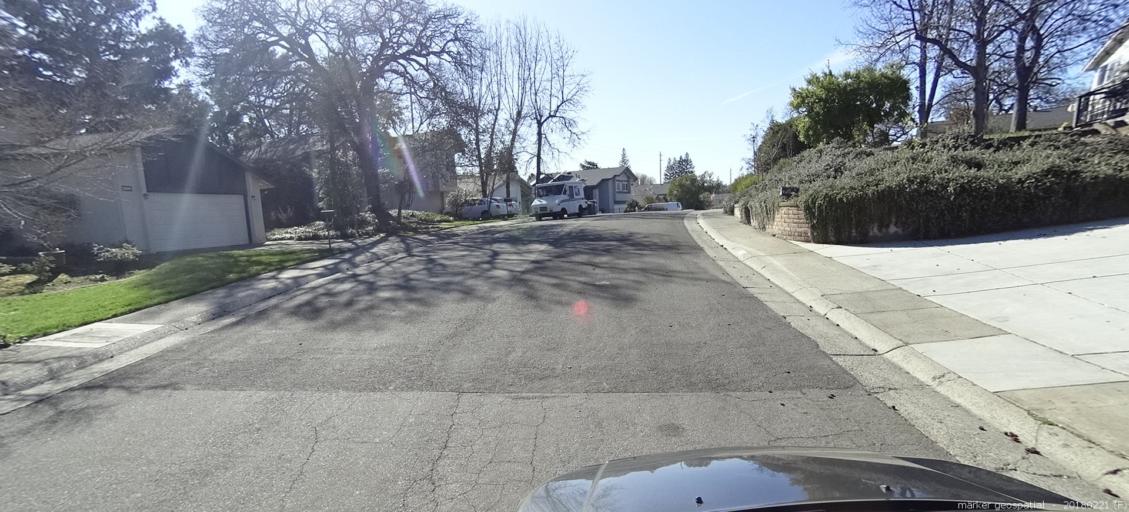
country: US
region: California
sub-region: Sacramento County
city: Orangevale
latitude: 38.6864
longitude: -121.2564
